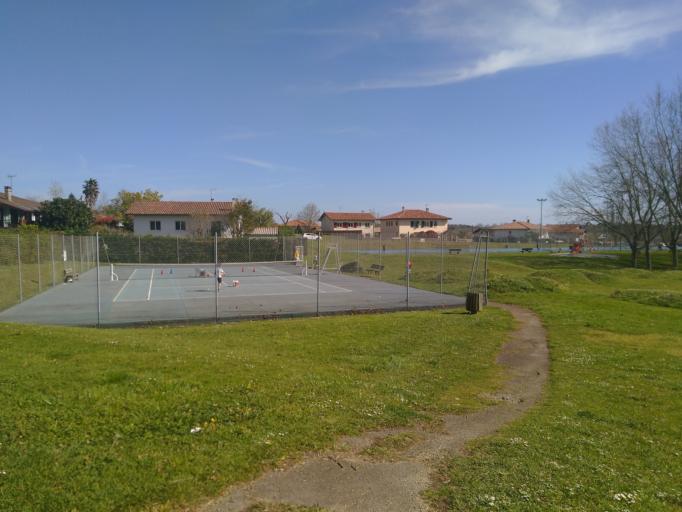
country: FR
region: Aquitaine
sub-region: Departement des Landes
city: Saint-Martin-de-Seignanx
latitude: 43.5439
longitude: -1.3914
